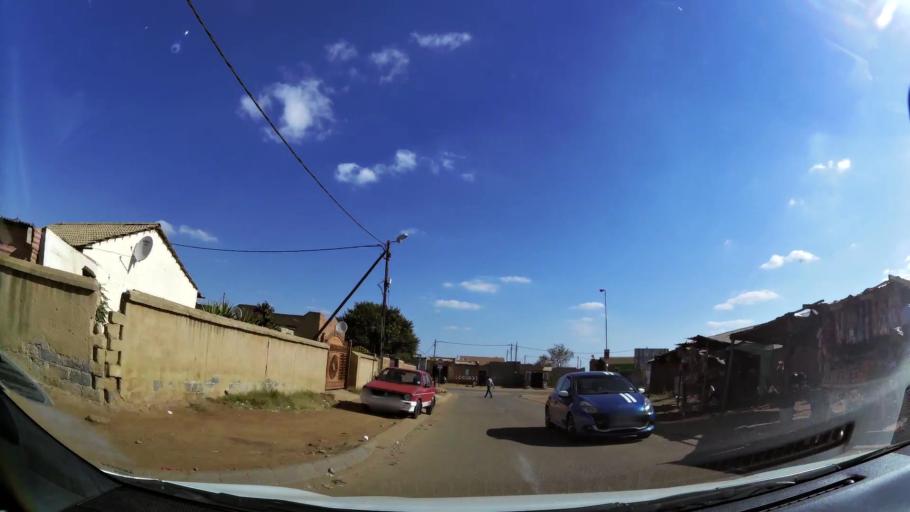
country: ZA
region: Gauteng
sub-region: City of Tshwane Metropolitan Municipality
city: Cullinan
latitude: -25.7154
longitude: 28.4069
